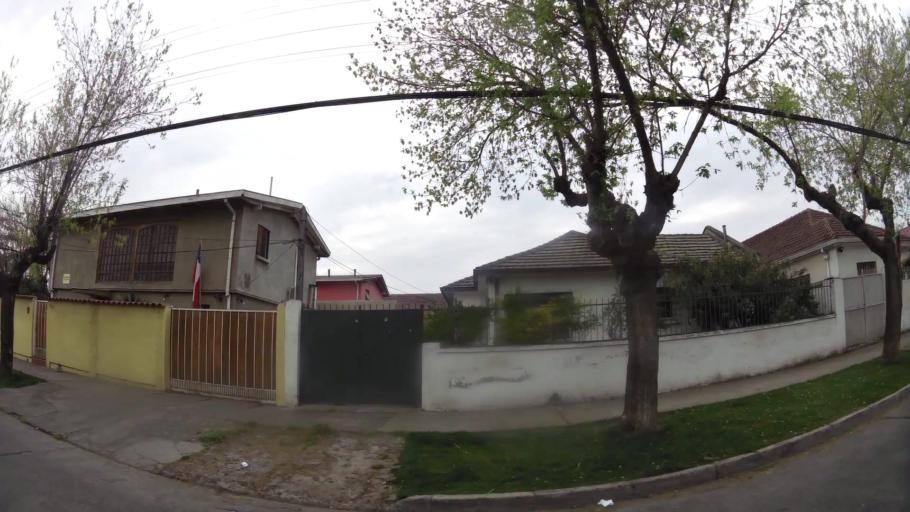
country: CL
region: Santiago Metropolitan
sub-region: Provincia de Santiago
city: Villa Presidente Frei, Nunoa, Santiago, Chile
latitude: -33.4612
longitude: -70.5917
